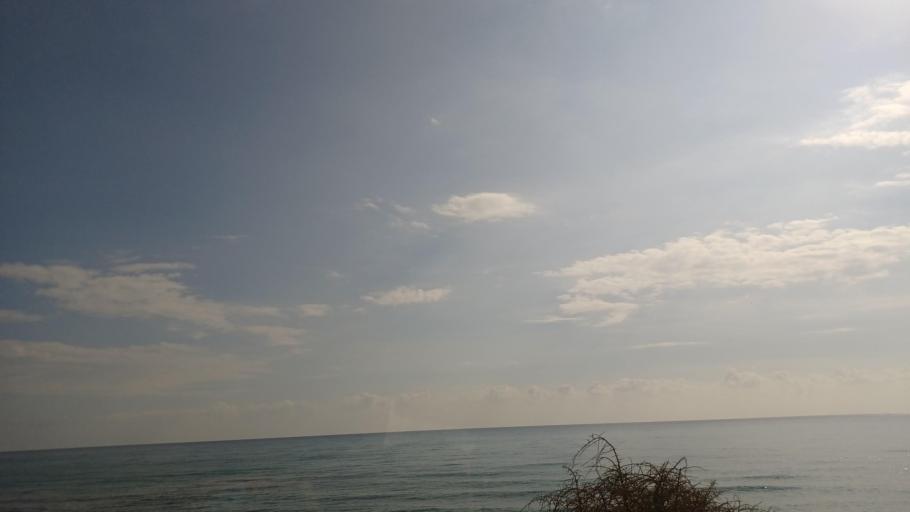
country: CY
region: Larnaka
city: Kofinou
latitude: 34.7670
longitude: 33.4400
